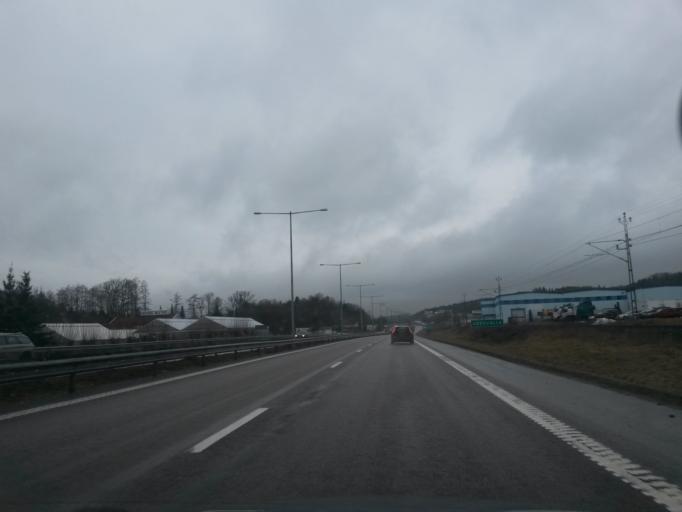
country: SE
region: Vaestra Goetaland
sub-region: Uddevalla Kommun
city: Uddevalla
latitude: 58.3522
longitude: 11.9747
